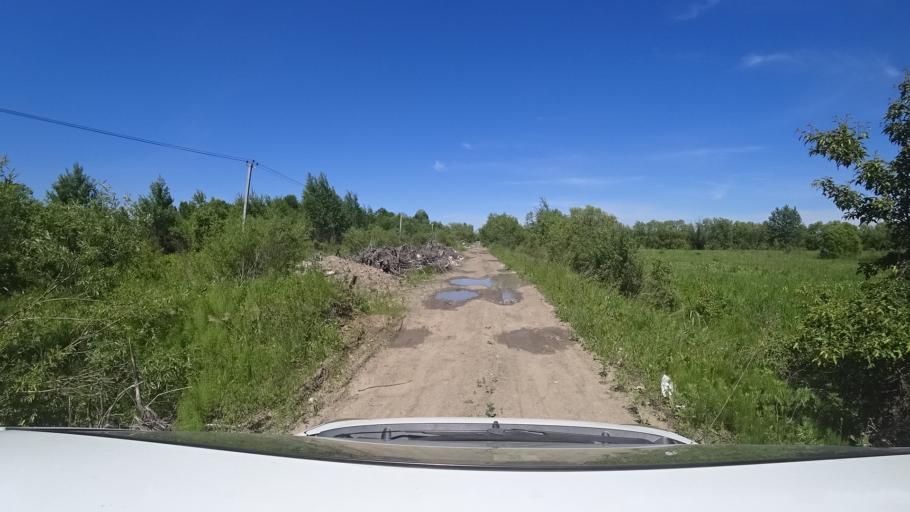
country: RU
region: Khabarovsk Krai
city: Topolevo
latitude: 48.4856
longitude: 135.1763
